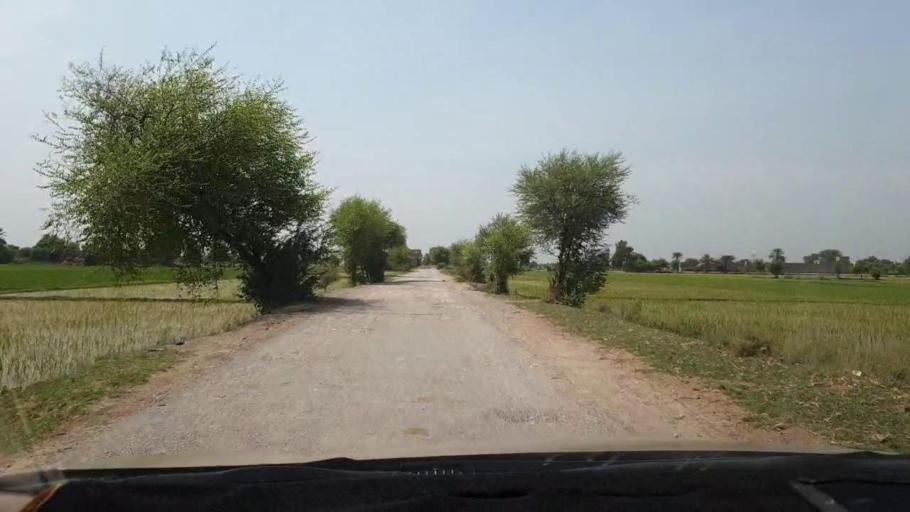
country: PK
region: Sindh
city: Naudero
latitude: 27.6411
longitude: 68.2738
